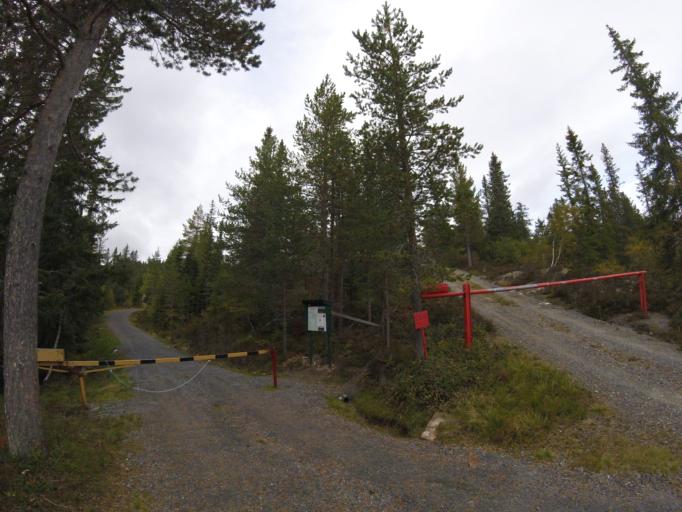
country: NO
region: Buskerud
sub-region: Flesberg
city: Lampeland
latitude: 59.7569
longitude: 9.4392
